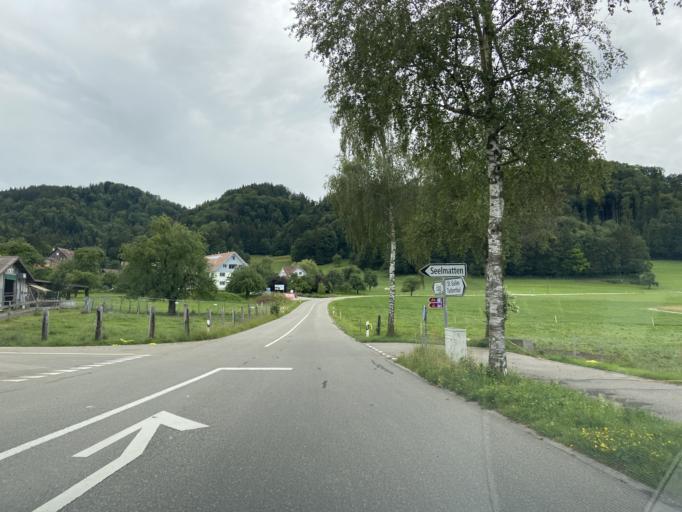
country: CH
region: Thurgau
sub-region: Muenchwilen District
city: Aadorf
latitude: 47.4546
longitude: 8.8962
